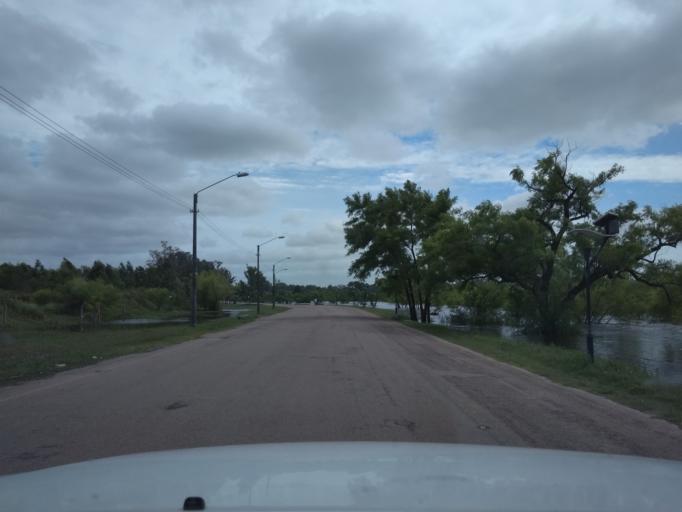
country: UY
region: Florida
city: Florida
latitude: -34.1052
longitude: -56.2043
